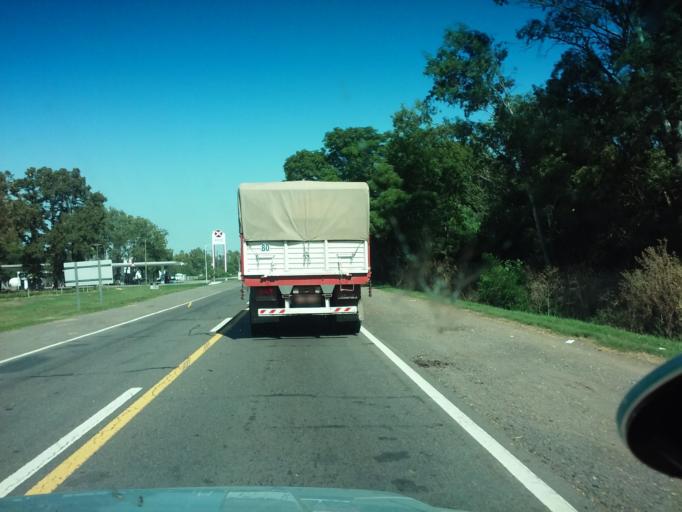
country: AR
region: Buenos Aires
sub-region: Partido de Alberti
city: Alberti
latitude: -35.0559
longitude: -60.2695
